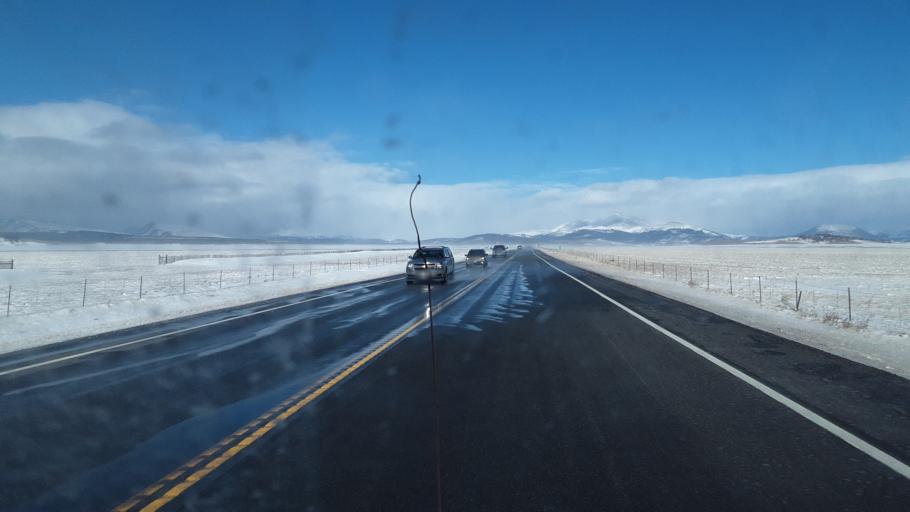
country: US
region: Colorado
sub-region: Park County
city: Fairplay
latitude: 39.1486
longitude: -105.9982
